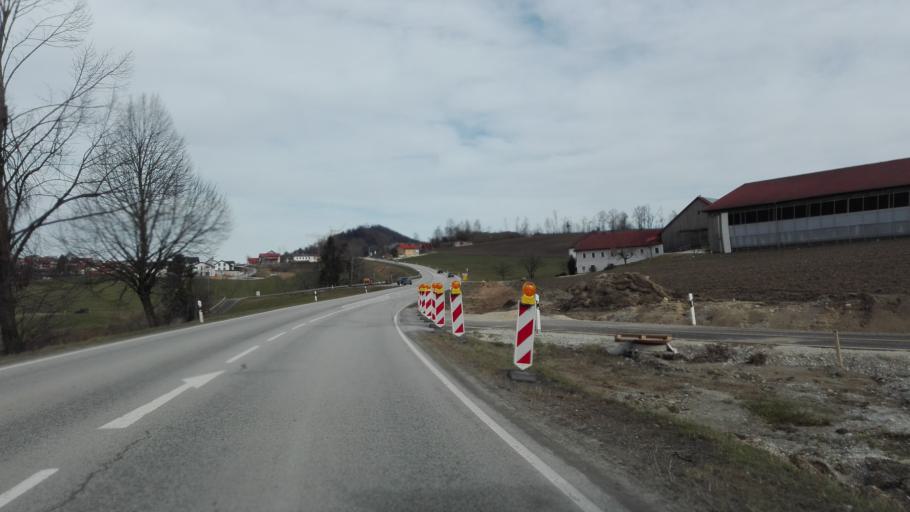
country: DE
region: Bavaria
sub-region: Lower Bavaria
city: Hauzenberg
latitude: 48.6468
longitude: 13.6119
